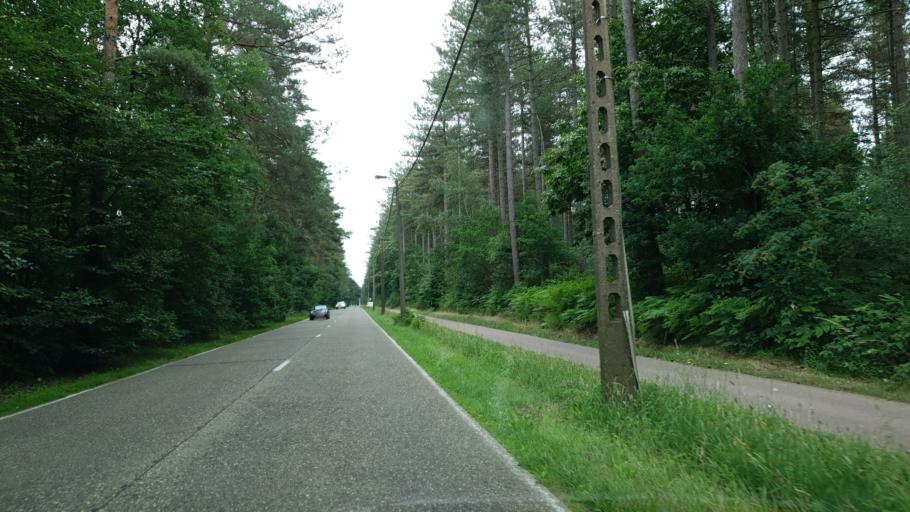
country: BE
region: Flanders
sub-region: Provincie Antwerpen
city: Westerlo
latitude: 51.0590
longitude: 4.9316
